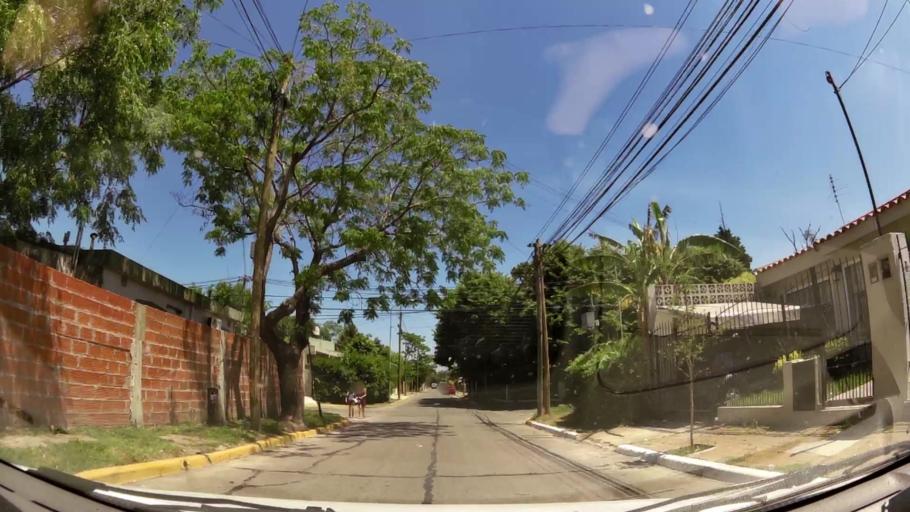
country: AR
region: Buenos Aires
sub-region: Partido de Merlo
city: Merlo
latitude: -34.6640
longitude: -58.7125
